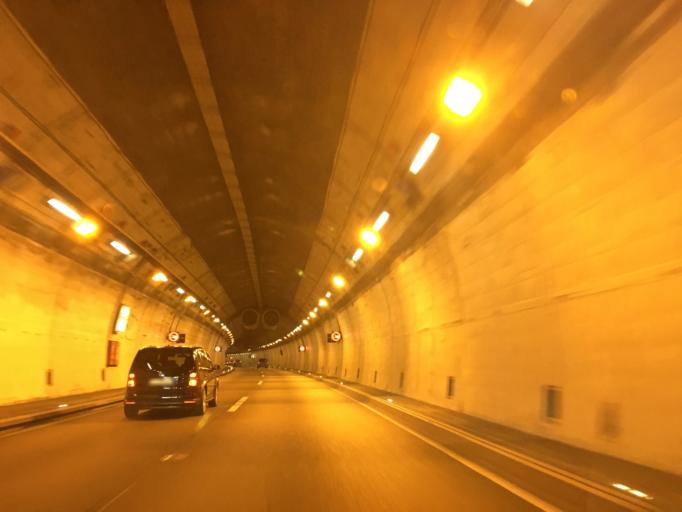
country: CH
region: Basel-Landschaft
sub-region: Bezirk Waldenburg
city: Diegten
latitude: 47.3787
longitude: 7.8162
